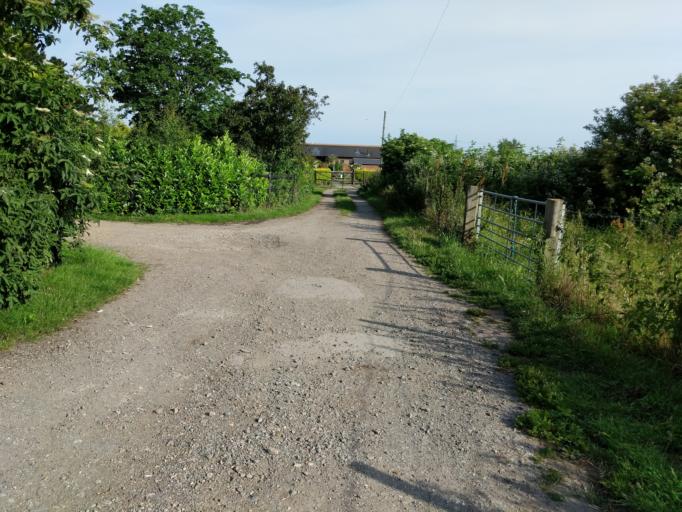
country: GB
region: England
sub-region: Kent
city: Faversham
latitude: 51.3312
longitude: 0.9151
